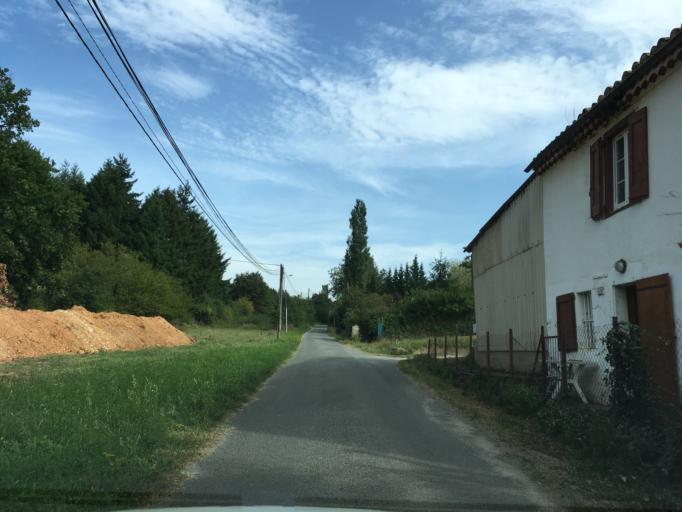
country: FR
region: Midi-Pyrenees
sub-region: Departement du Tarn
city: Castres
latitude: 43.6067
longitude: 2.2776
